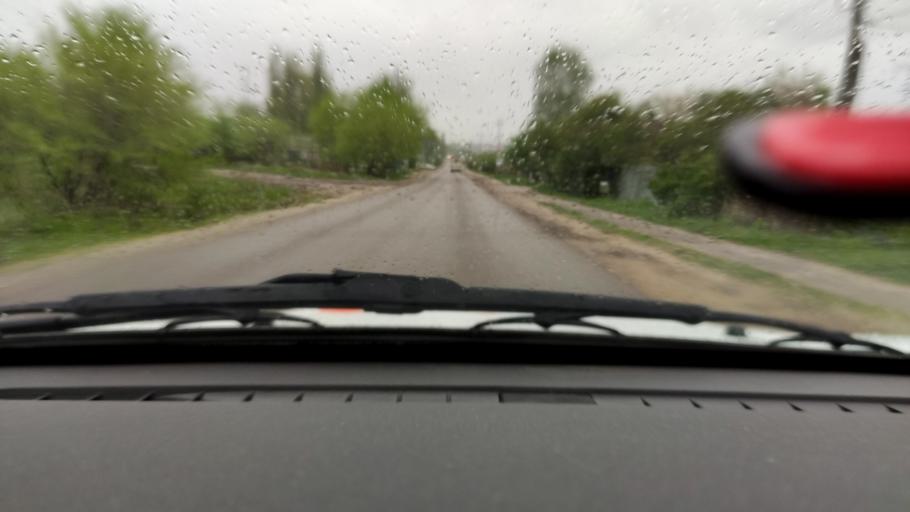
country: RU
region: Voronezj
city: Strelitsa
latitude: 51.6221
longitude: 38.9121
